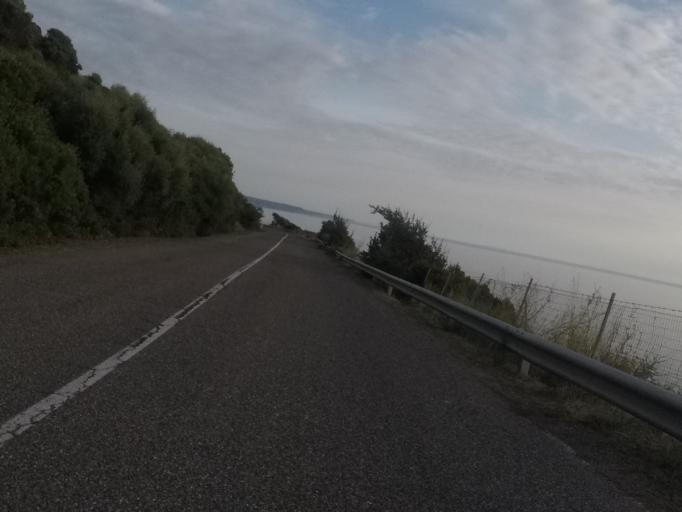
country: IT
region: Sardinia
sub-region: Provincia di Oristano
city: Bosa
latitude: 40.3371
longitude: 8.4298
